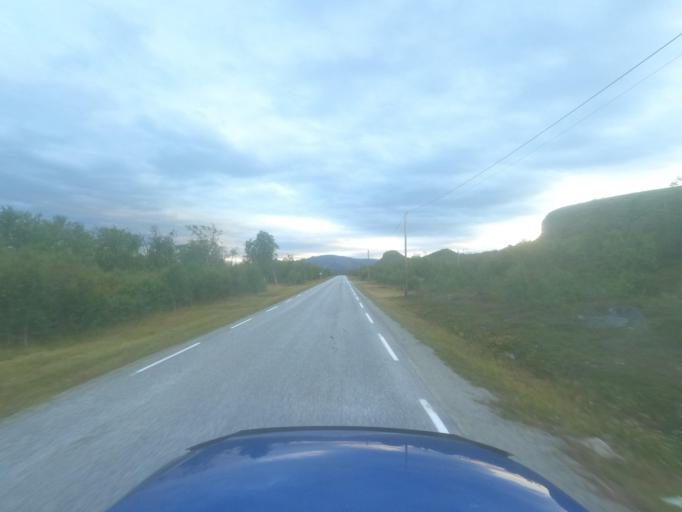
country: NO
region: Finnmark Fylke
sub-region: Porsanger
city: Lakselv
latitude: 70.1925
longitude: 24.9167
